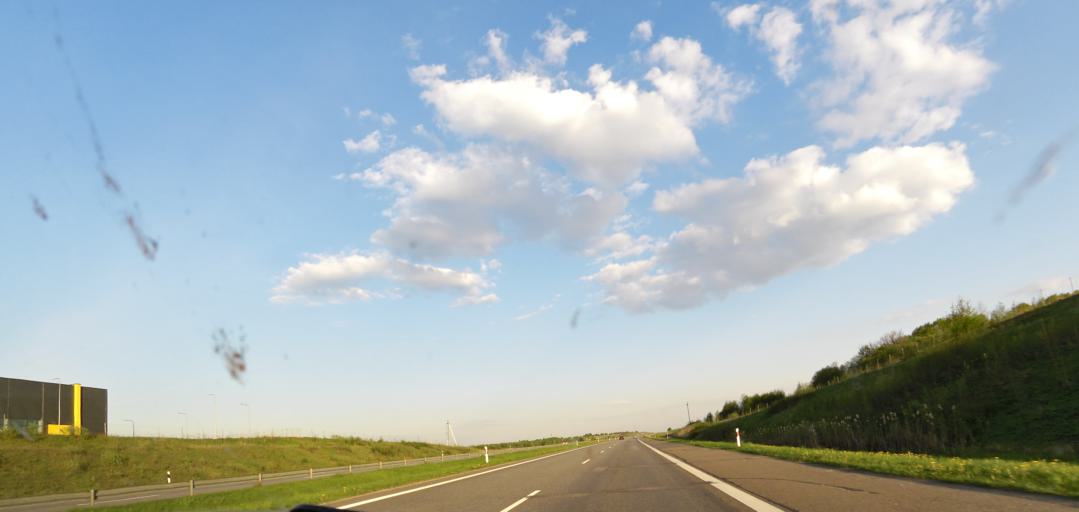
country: LT
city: Sirvintos
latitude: 54.8943
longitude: 25.0500
